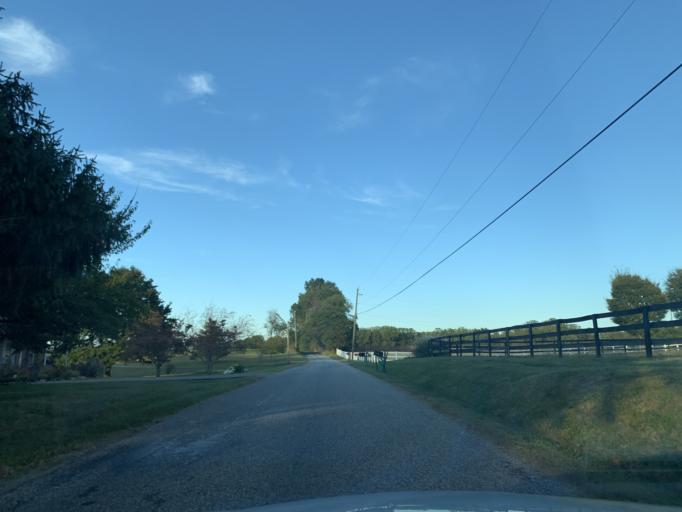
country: US
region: Maryland
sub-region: Harford County
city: Fallston
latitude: 39.4948
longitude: -76.4516
